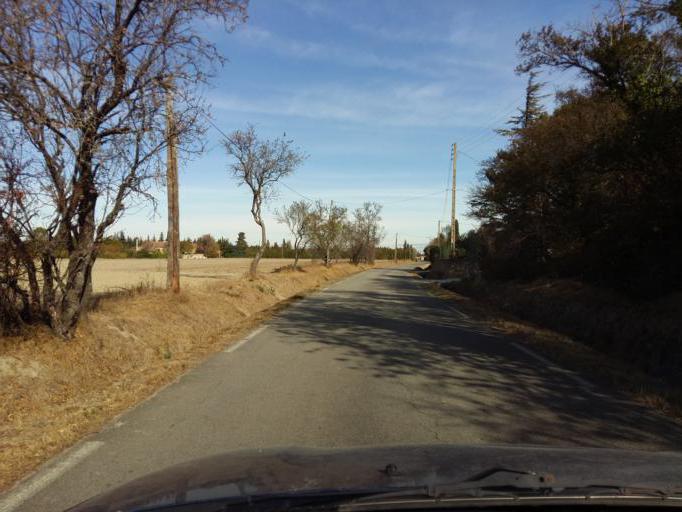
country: FR
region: Provence-Alpes-Cote d'Azur
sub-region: Departement du Vaucluse
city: Orange
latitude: 44.1556
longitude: 4.8349
